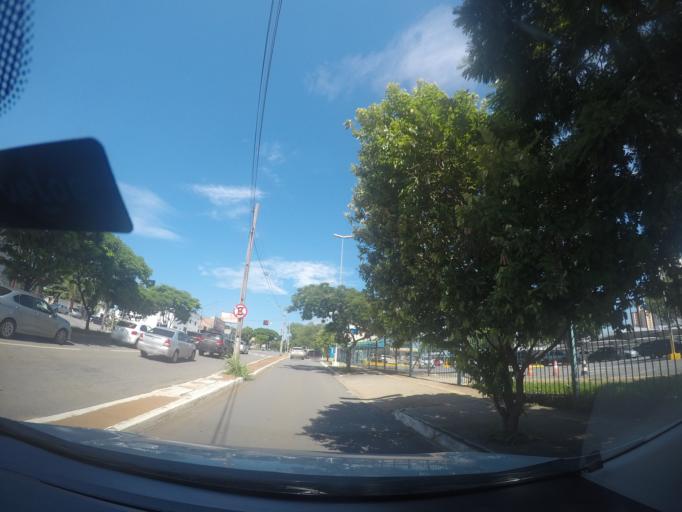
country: BR
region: Goias
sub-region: Goiania
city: Goiania
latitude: -16.7103
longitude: -49.2966
